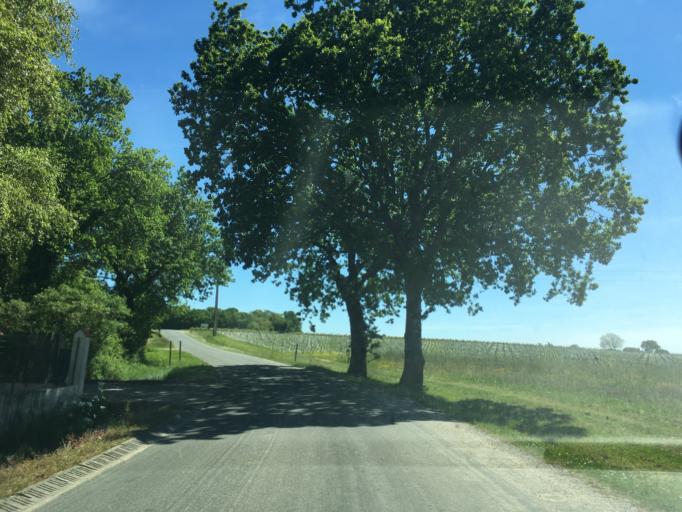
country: FR
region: Aquitaine
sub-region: Departement de la Gironde
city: Lesparre-Medoc
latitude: 45.3195
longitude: -0.8816
